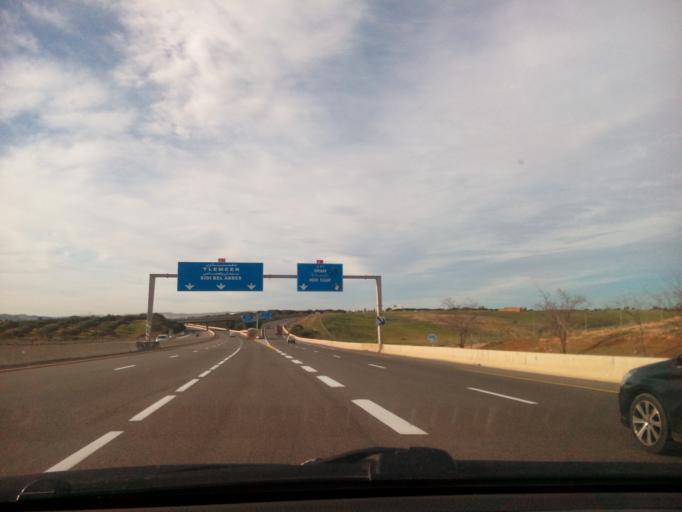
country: DZ
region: Mascara
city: Sig
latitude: 35.5449
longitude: -0.3401
